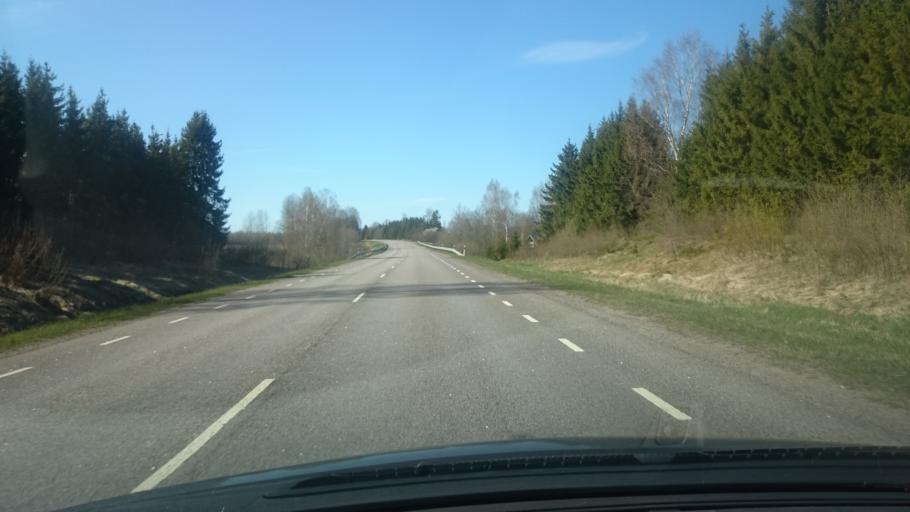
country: EE
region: Polvamaa
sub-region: Polva linn
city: Polva
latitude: 58.2385
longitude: 27.0152
